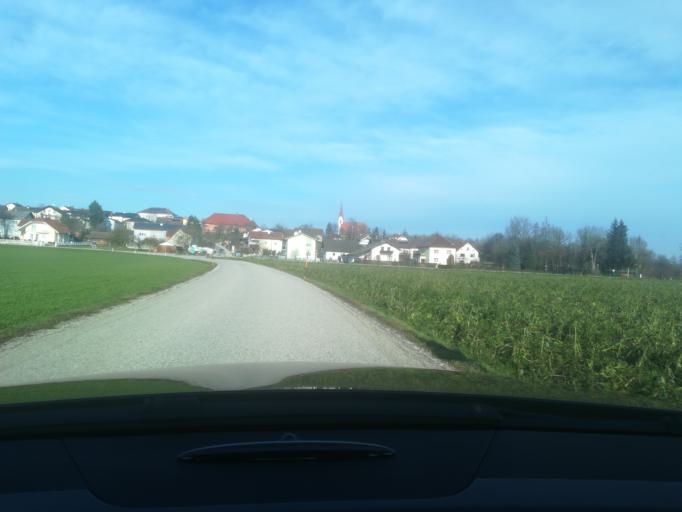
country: AT
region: Upper Austria
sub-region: Wels-Land
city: Holzhausen
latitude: 48.2193
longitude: 14.0985
